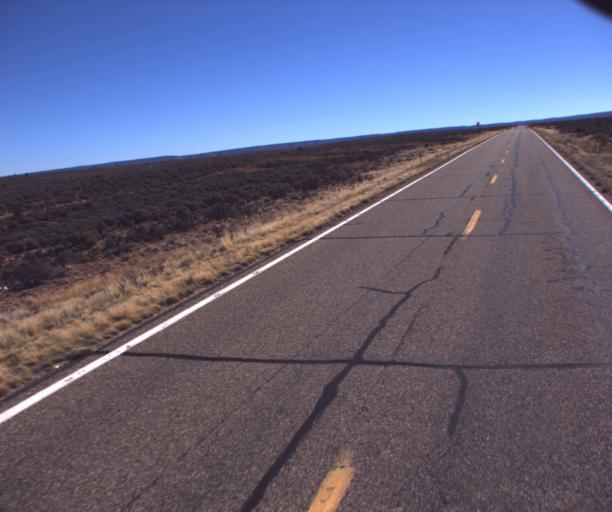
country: US
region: Arizona
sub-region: Coconino County
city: Fredonia
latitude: 36.9009
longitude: -112.3773
